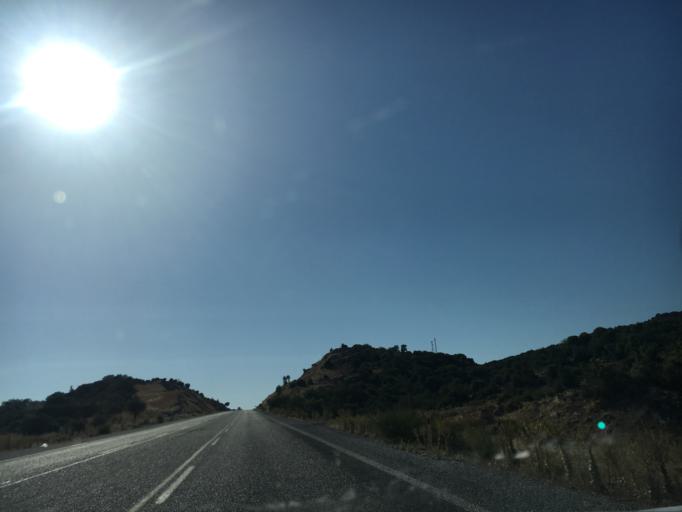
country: TR
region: Canakkale
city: Behram
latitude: 39.5065
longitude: 26.3935
